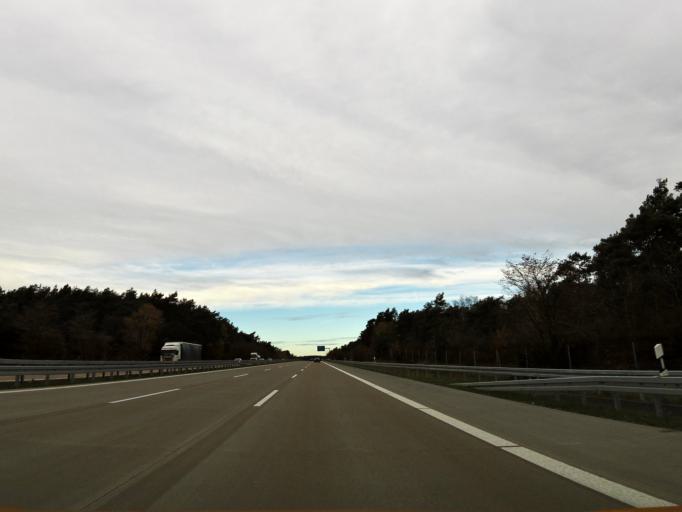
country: DE
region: Brandenburg
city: Golzow
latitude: 52.3450
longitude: 12.6232
